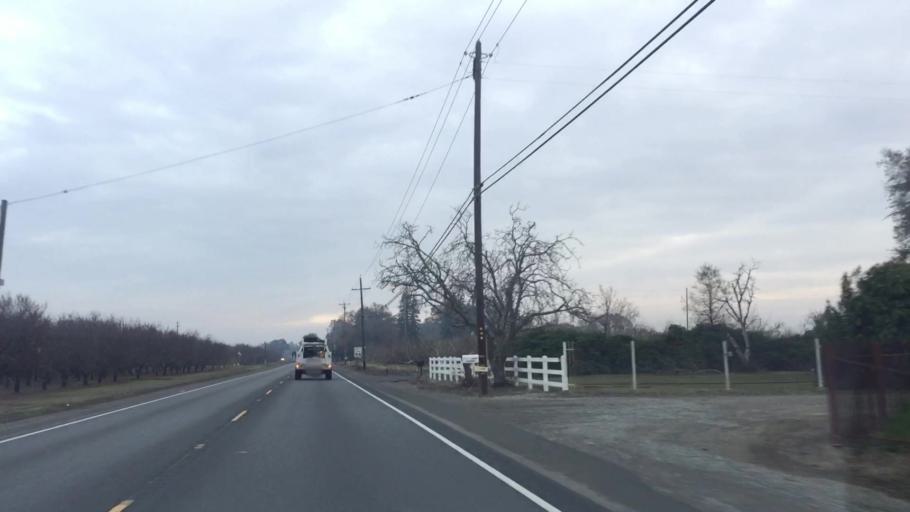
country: US
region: California
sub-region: Sutter County
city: Live Oak
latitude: 39.2676
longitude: -121.5968
